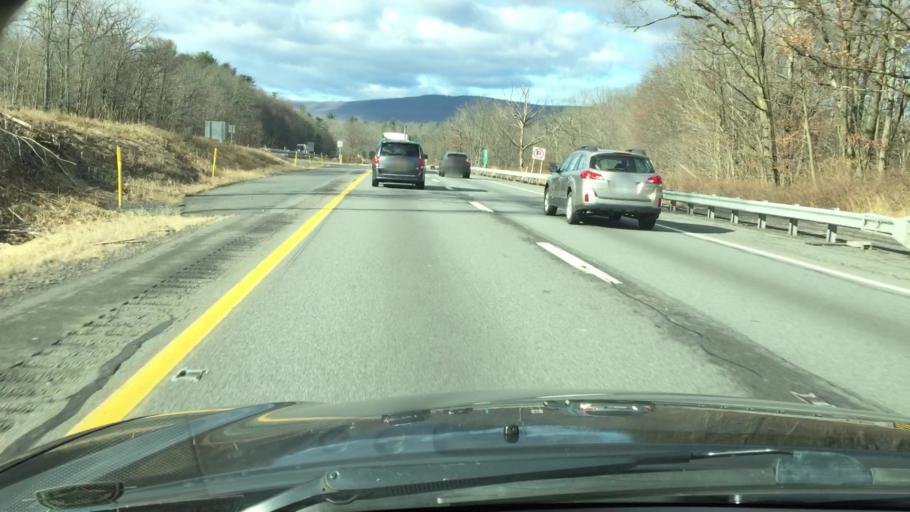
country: US
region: Pennsylvania
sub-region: Monroe County
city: Tannersville
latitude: 41.0086
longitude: -75.2910
